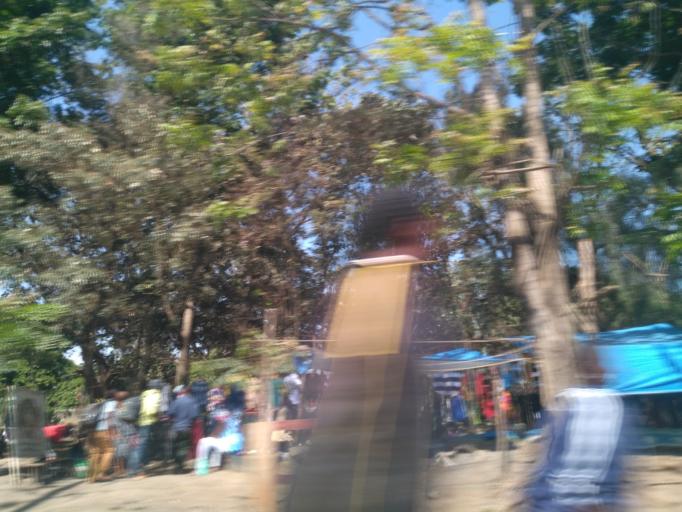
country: TZ
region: Arusha
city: Arusha
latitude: -3.3695
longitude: 36.6851
